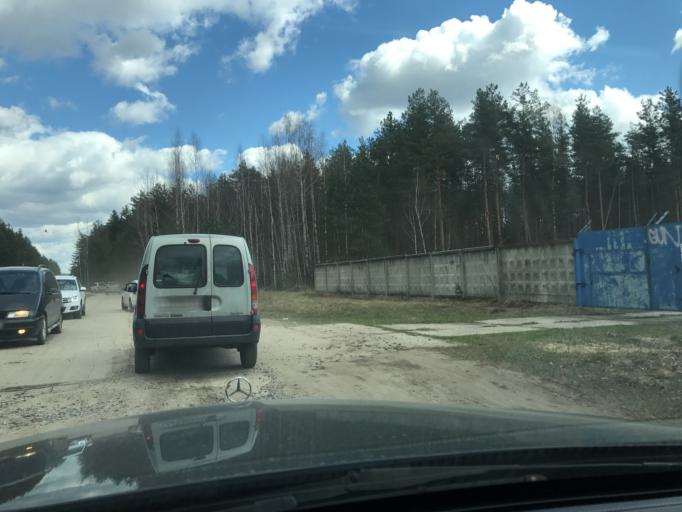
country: RU
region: Vladimir
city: Pokrov
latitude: 55.8660
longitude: 39.2274
